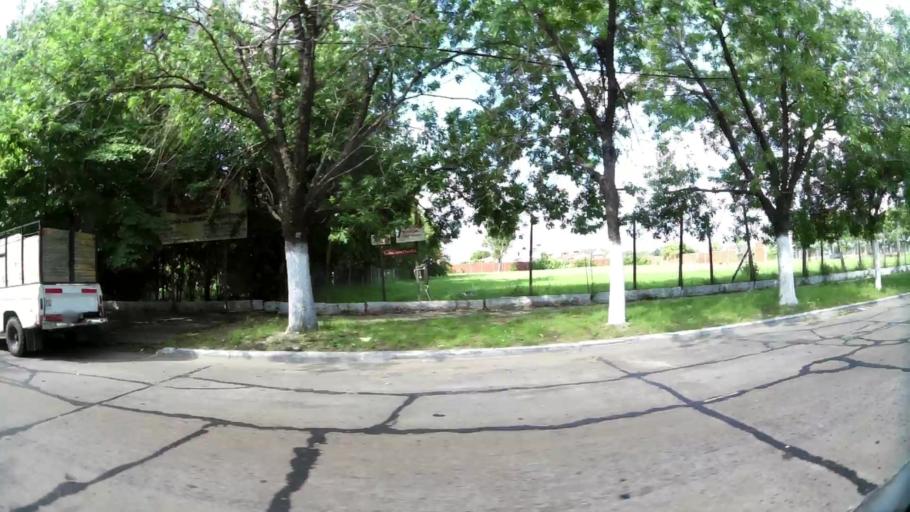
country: AR
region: Buenos Aires
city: San Justo
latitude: -34.6645
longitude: -58.5727
